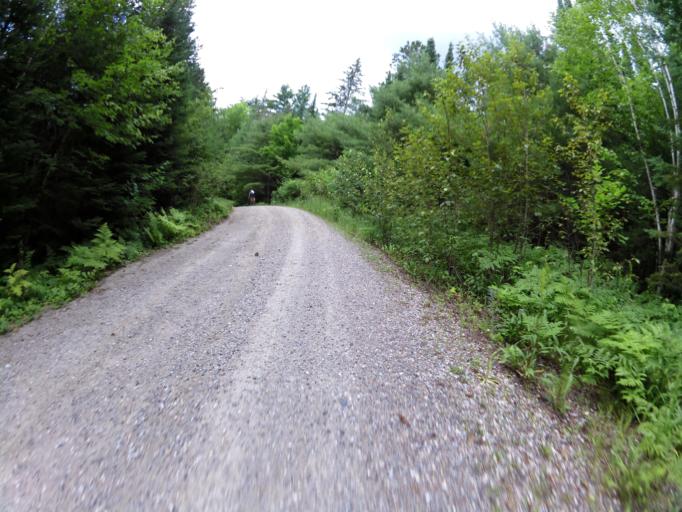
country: CA
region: Ontario
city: Perth
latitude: 45.0106
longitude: -76.5926
